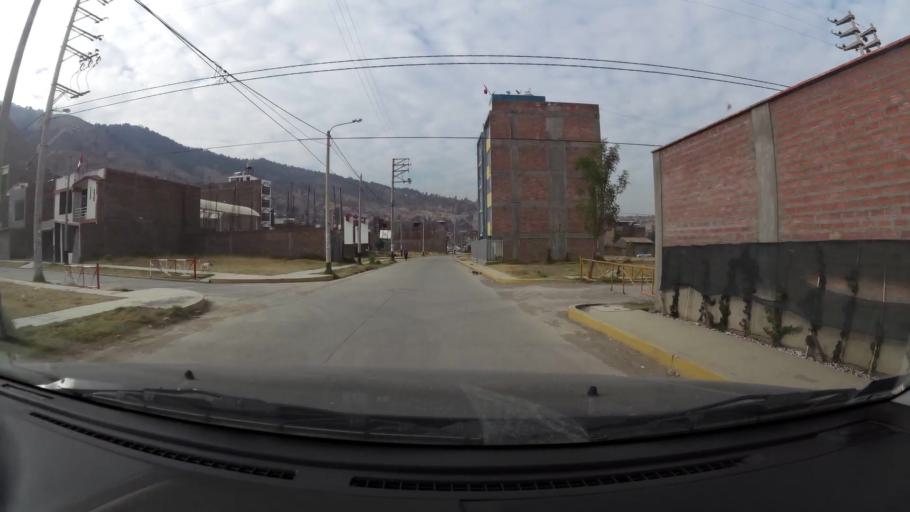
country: PE
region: Junin
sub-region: Provincia de Huancayo
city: Huancayo
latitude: -12.0492
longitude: -75.1890
